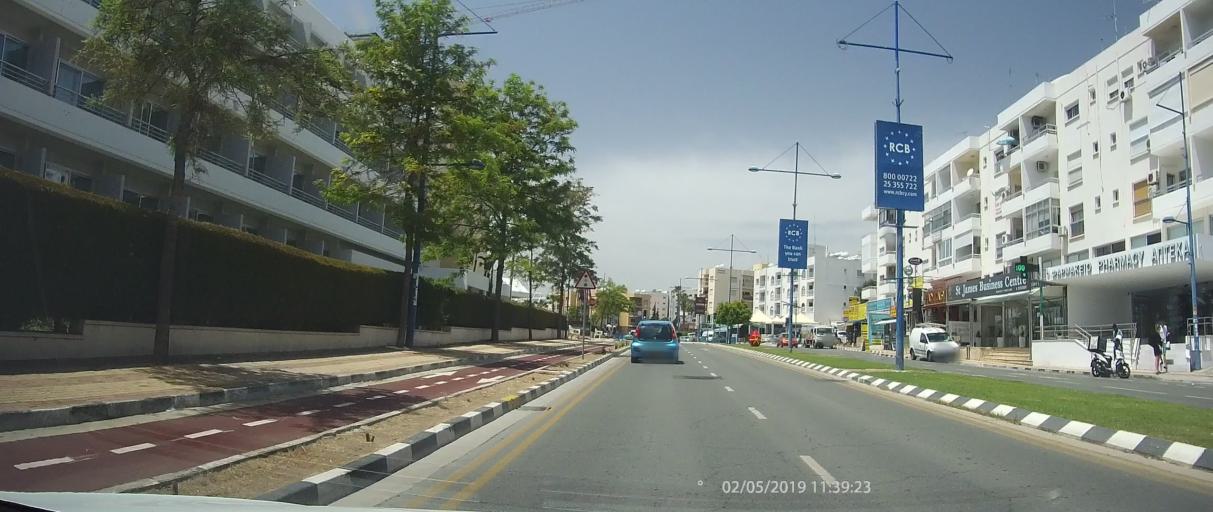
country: CY
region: Larnaka
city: Agios Tychon
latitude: 34.7100
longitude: 33.1304
